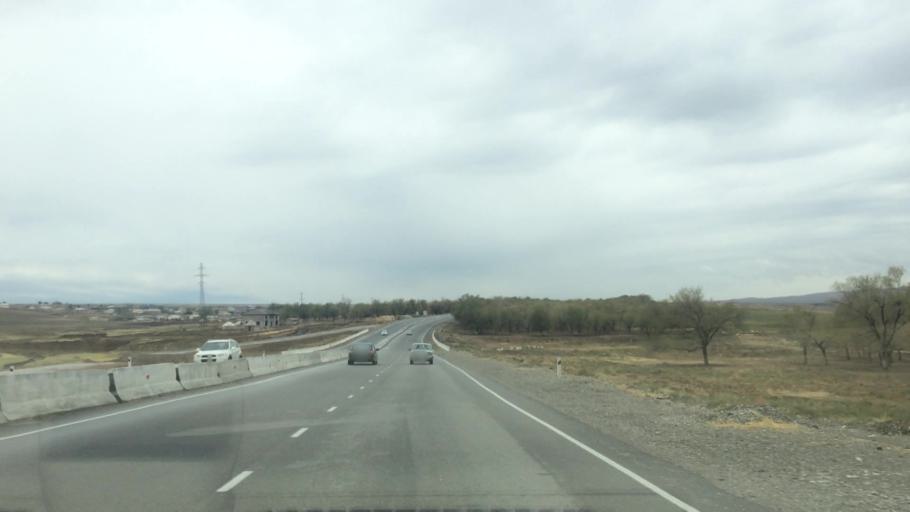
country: UZ
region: Samarqand
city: Bulung'ur
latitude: 39.9217
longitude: 67.5165
